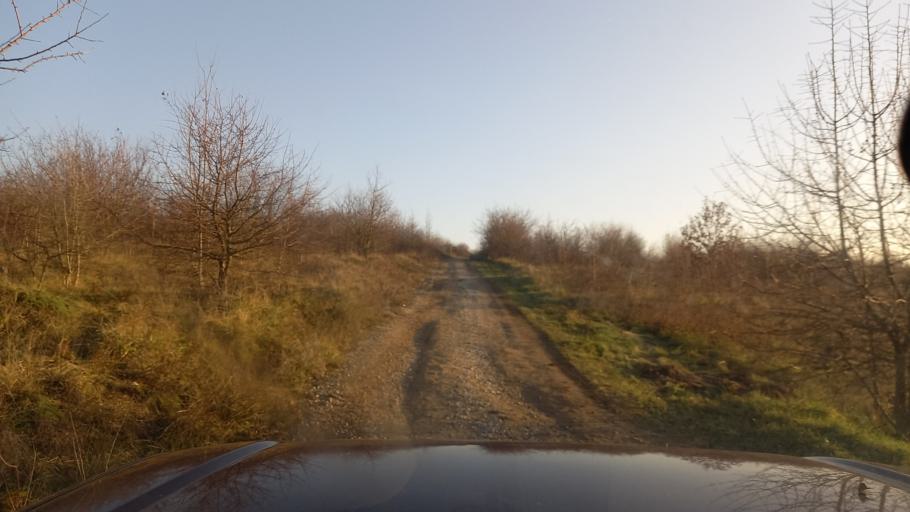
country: RU
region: Krasnodarskiy
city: Azovskaya
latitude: 44.8115
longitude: 38.5947
